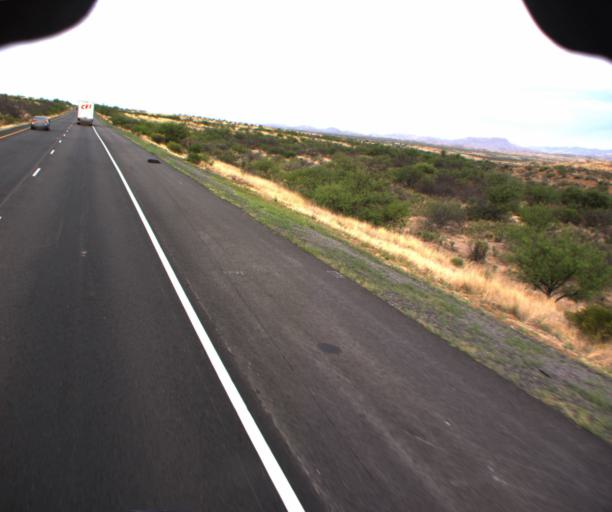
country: US
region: Arizona
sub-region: Cochise County
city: Mescal
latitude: 31.9721
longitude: -110.4821
